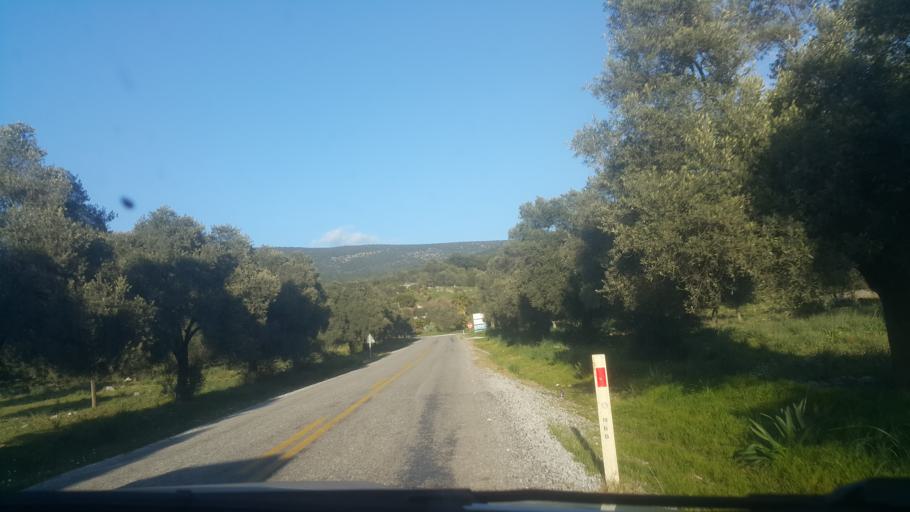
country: TR
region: Mugla
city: Kiulukioi
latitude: 37.3040
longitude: 27.6114
